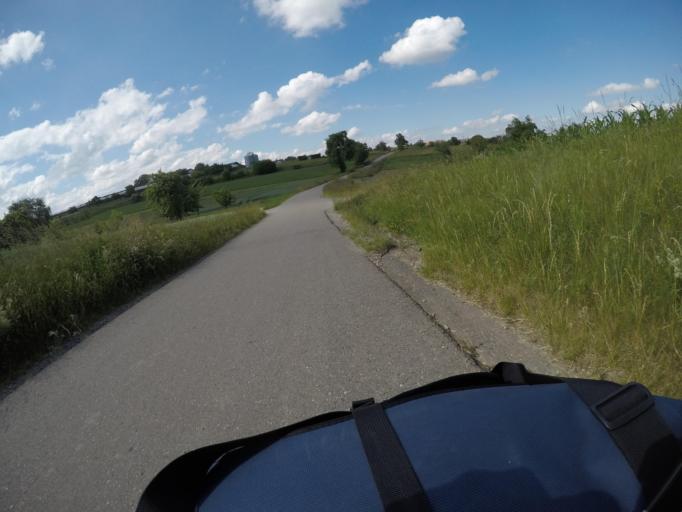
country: DE
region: Baden-Wuerttemberg
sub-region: Regierungsbezirk Stuttgart
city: Herrenberg
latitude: 48.6014
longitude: 8.8337
